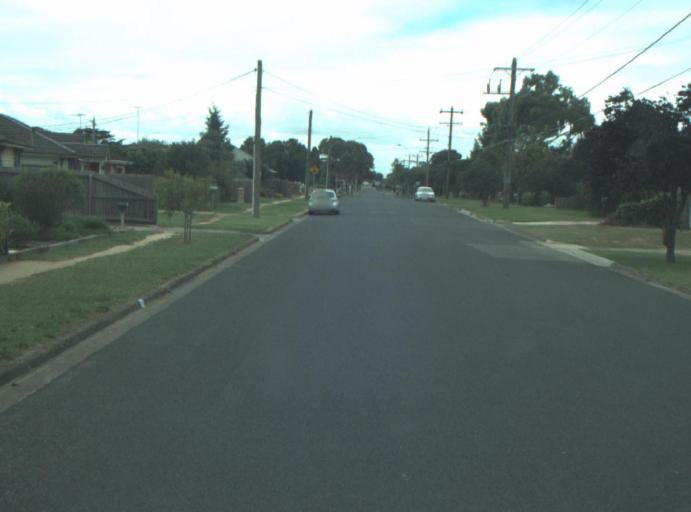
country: AU
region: Victoria
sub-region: Greater Geelong
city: Lara
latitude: -38.0167
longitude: 144.4038
